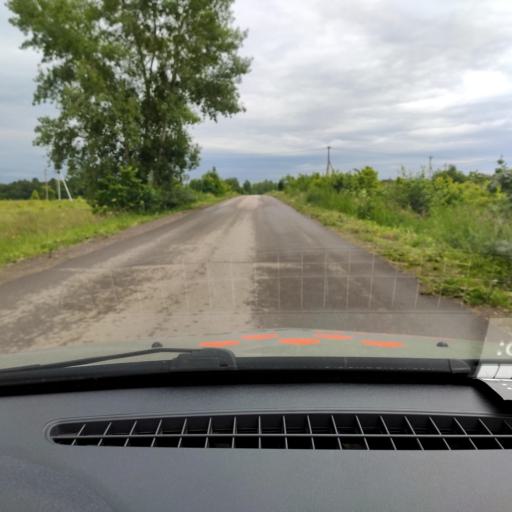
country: RU
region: Bashkortostan
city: Iglino
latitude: 54.8960
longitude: 56.2761
